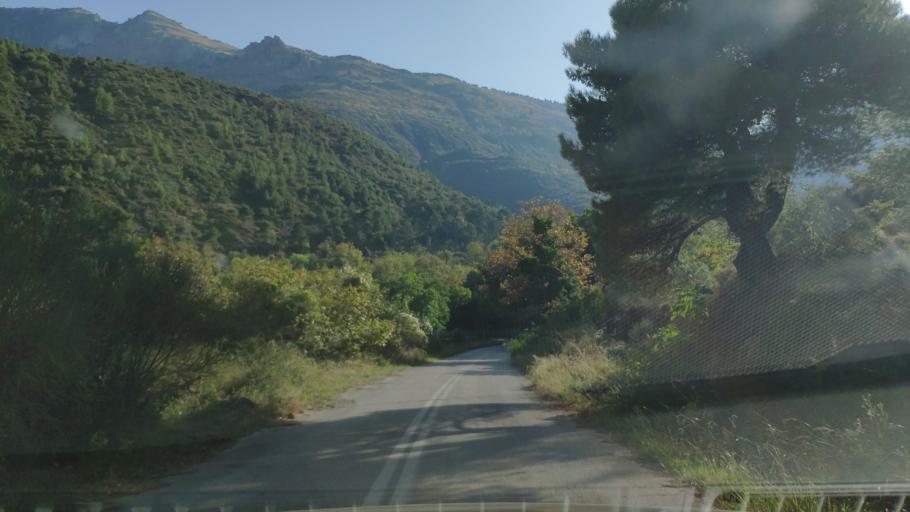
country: GR
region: West Greece
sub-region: Nomos Achaias
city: Aiyira
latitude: 38.0692
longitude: 22.3925
